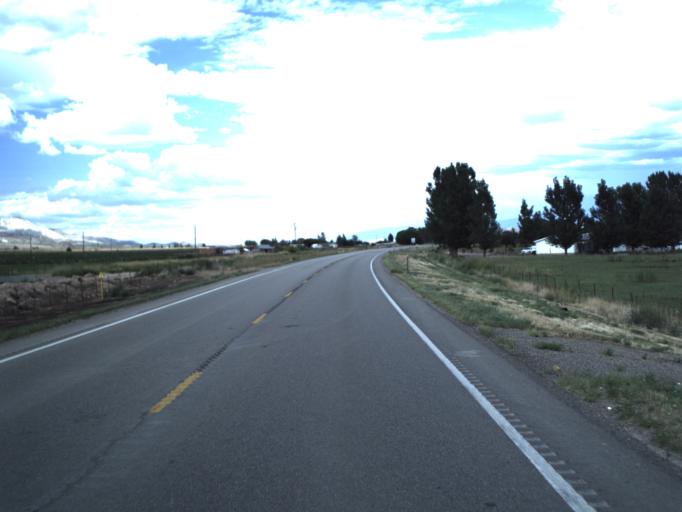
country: US
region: Utah
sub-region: Sevier County
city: Richfield
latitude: 38.7809
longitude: -112.0606
